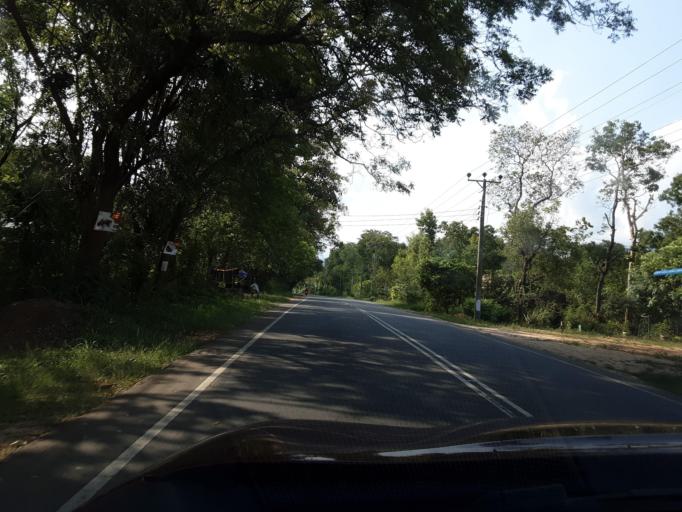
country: LK
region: Uva
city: Haputale
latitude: 6.6091
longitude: 81.1343
